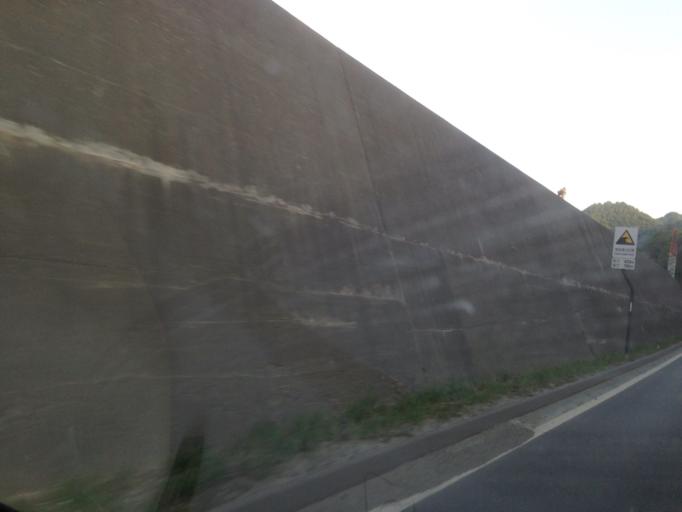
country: JP
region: Iwate
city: Kamaishi
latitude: 39.3076
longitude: 141.8904
